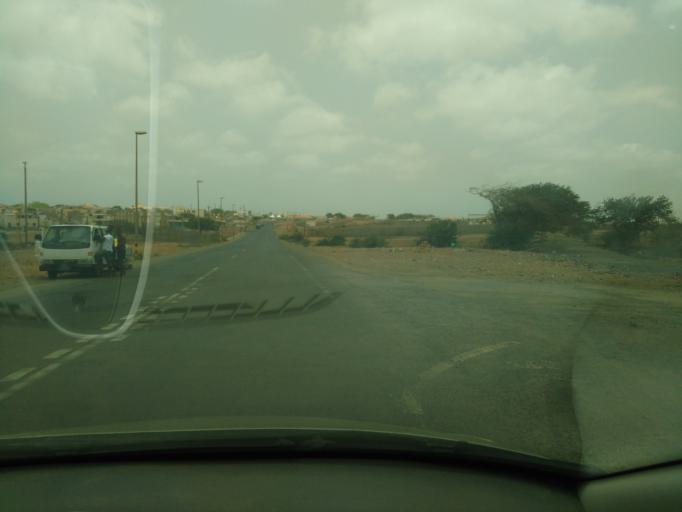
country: CV
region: Sal
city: Espargos
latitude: 16.7557
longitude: -22.9501
